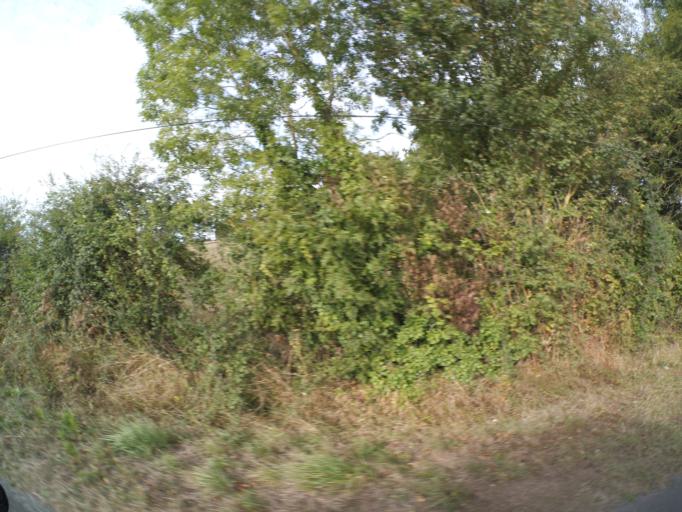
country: FR
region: Pays de la Loire
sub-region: Departement de Maine-et-Loire
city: La Chapelle-du-Genet
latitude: 47.1826
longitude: -1.0413
